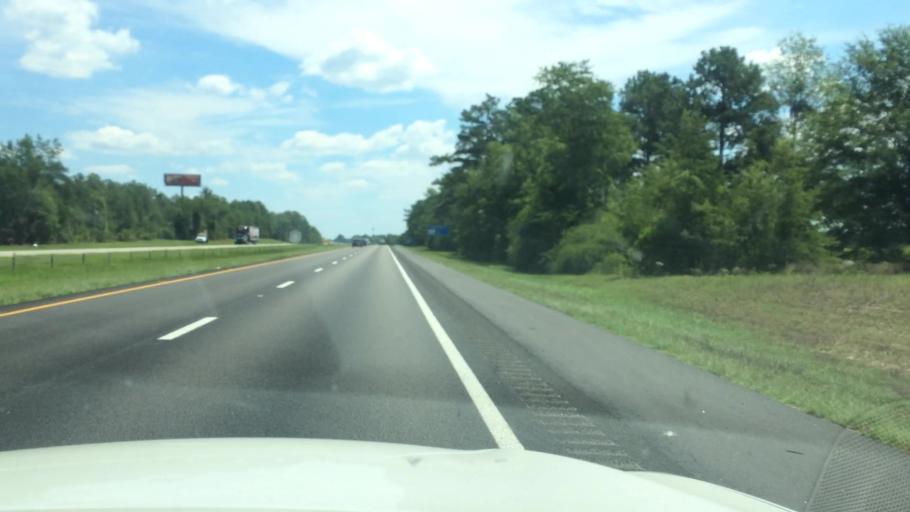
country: US
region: South Carolina
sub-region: Aiken County
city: Aiken
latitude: 33.6580
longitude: -81.6934
